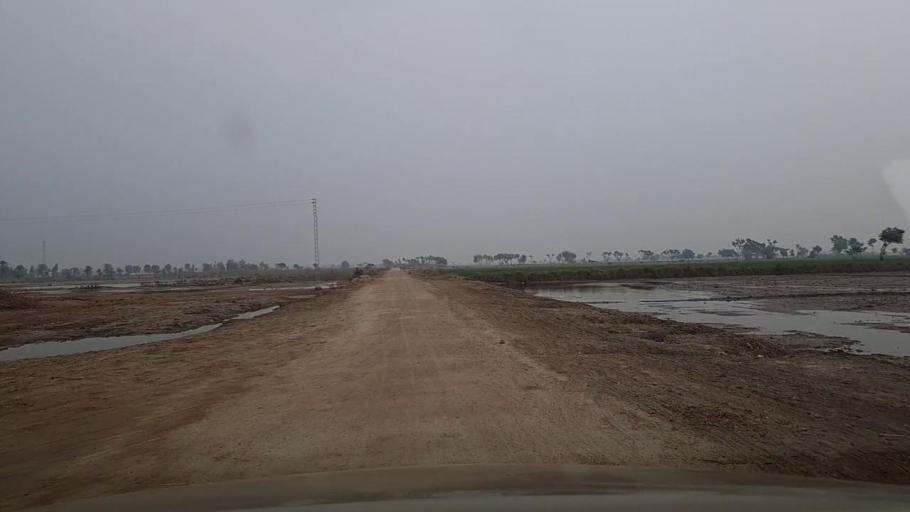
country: PK
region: Sindh
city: Sanghar
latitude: 26.1190
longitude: 68.9171
